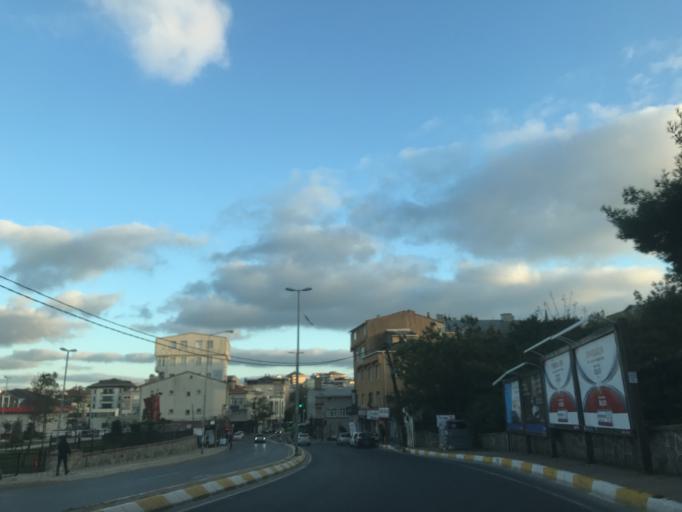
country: TR
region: Istanbul
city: Sisli
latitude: 41.1331
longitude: 29.0394
